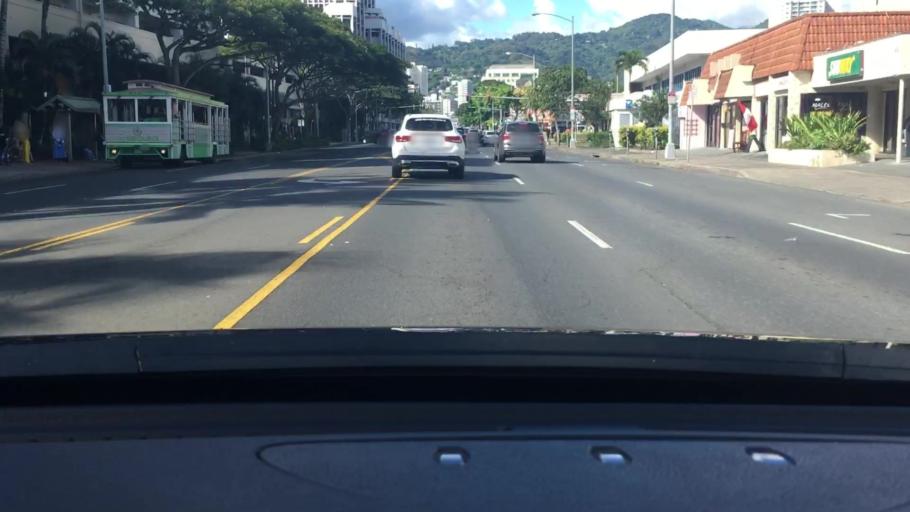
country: US
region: Hawaii
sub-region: Honolulu County
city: Honolulu
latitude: 21.2945
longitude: -157.8419
